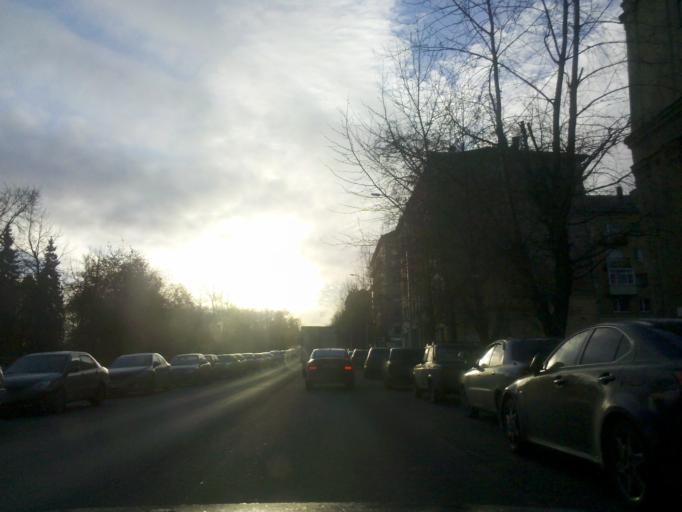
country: RU
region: Republic of Karelia
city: Petrozavodsk
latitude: 61.7933
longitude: 34.3773
